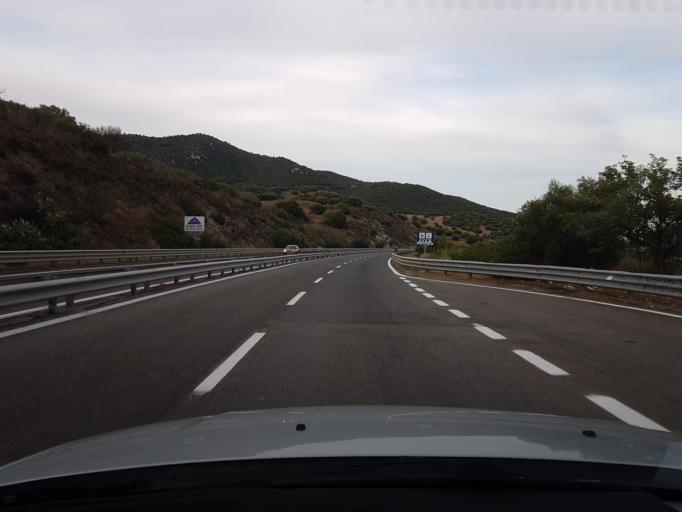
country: IT
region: Sardinia
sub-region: Provincia di Nuoro
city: Orune
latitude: 40.3669
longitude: 9.3709
